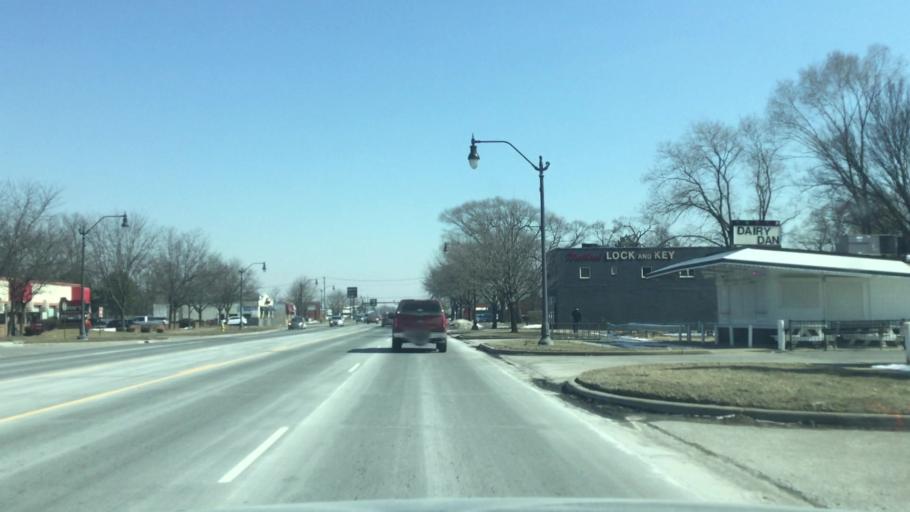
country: US
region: Michigan
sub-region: Wayne County
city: Westland
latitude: 42.3243
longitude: -83.3932
